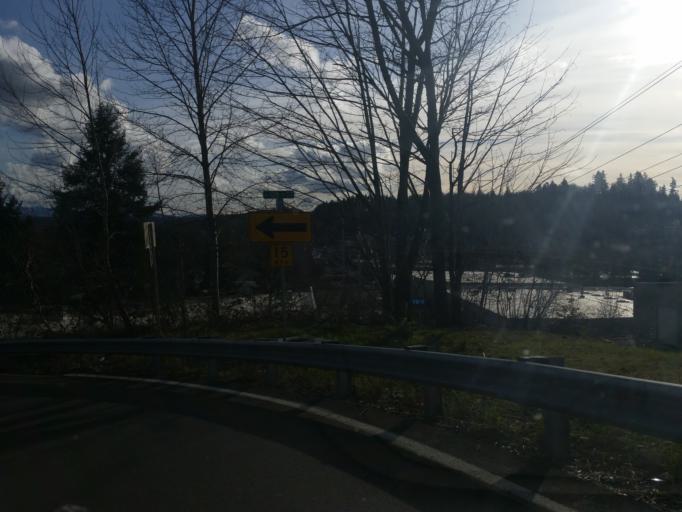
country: US
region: Washington
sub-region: King County
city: Kingsgate
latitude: 47.7153
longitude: -122.1589
